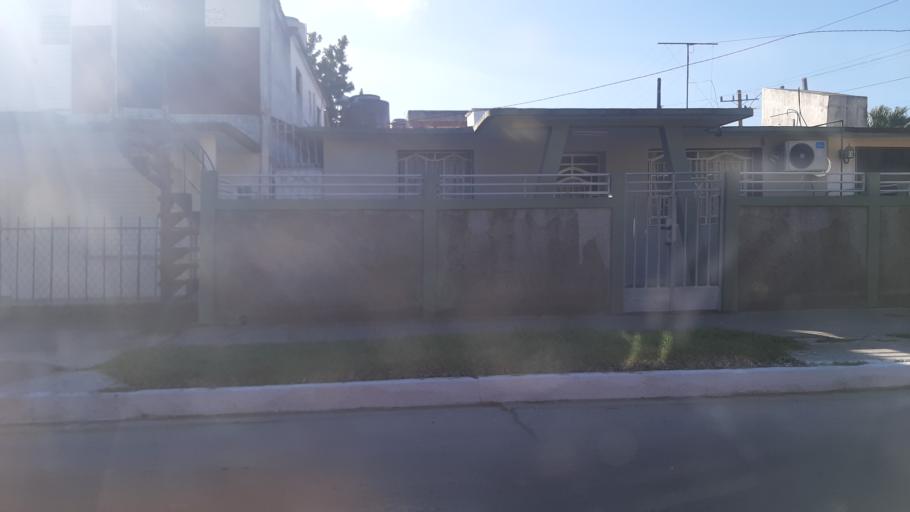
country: CU
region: Villa Clara
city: Santa Clara
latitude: 22.4122
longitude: -79.9560
